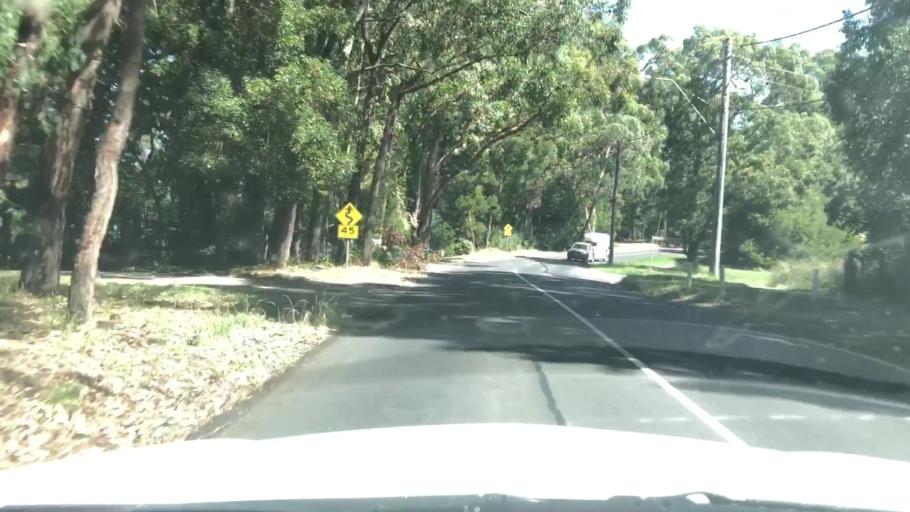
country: AU
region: Victoria
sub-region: Yarra Ranges
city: Macclesfield
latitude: -37.8911
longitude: 145.4756
